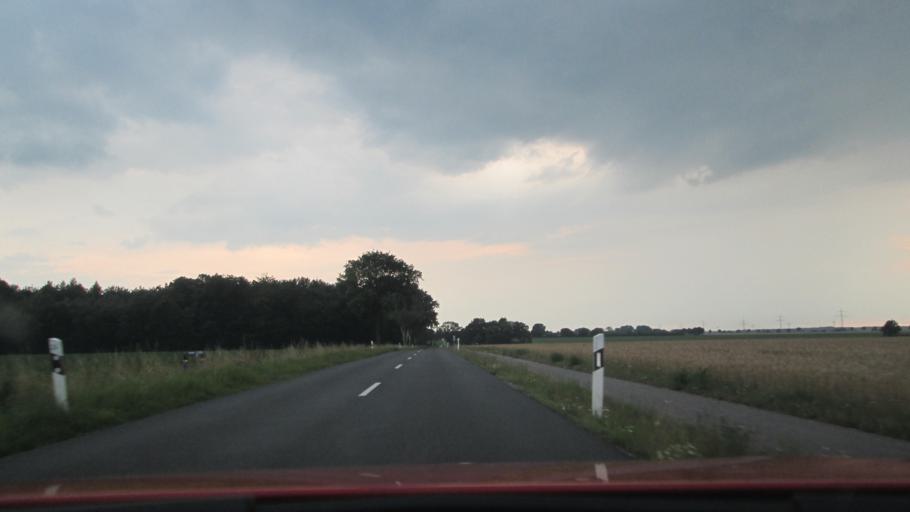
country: DE
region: Lower Saxony
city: Lehre
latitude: 52.3686
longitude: 10.6676
